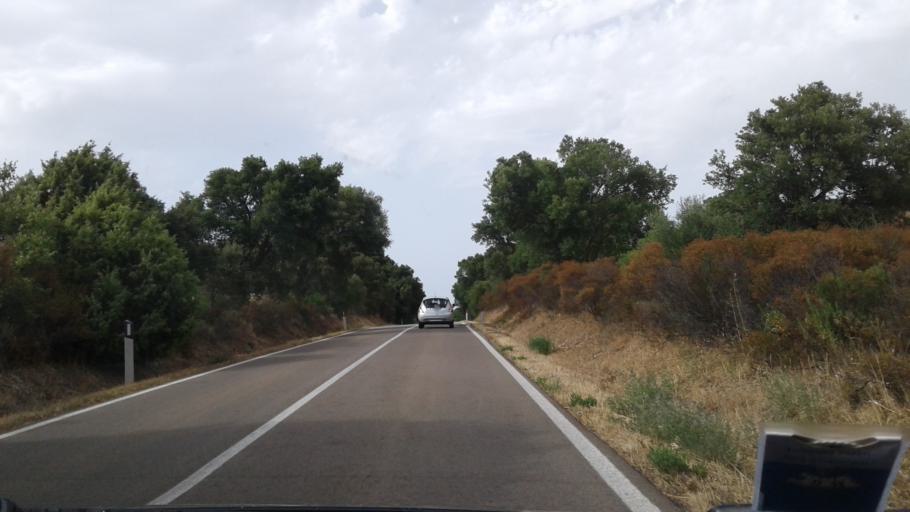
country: IT
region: Sardinia
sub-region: Provincia di Olbia-Tempio
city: Sant'Antonio di Gallura
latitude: 40.9543
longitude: 9.2943
